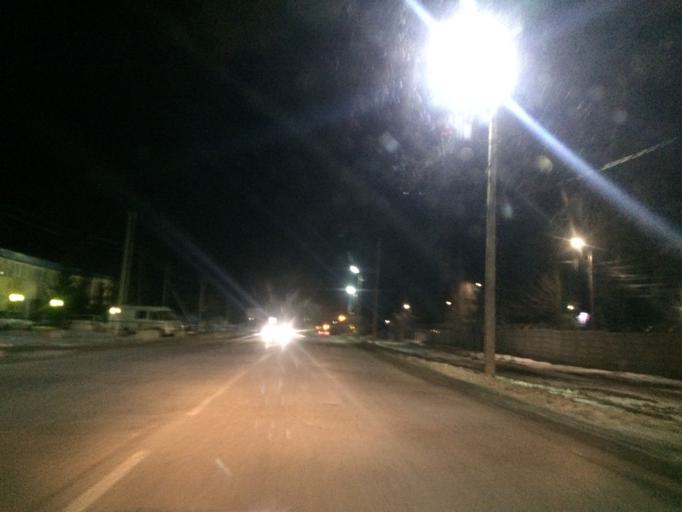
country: RU
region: Tula
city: Mendeleyevskiy
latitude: 54.1435
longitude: 37.5832
